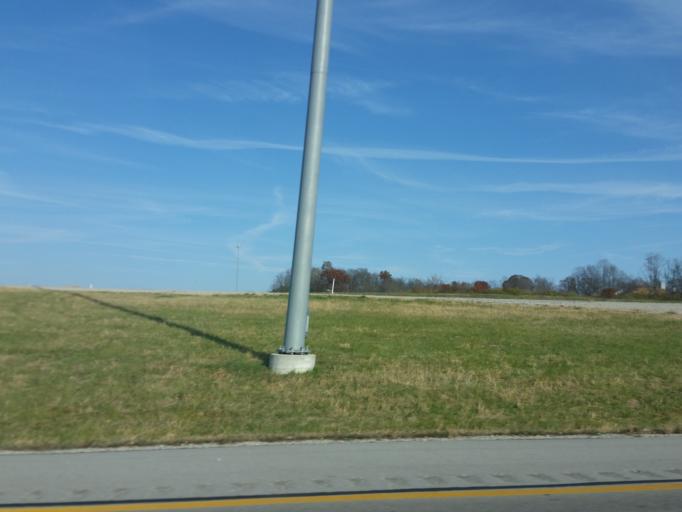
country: US
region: Kentucky
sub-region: Campbell County
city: Highland Heights
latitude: 39.0441
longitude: -84.4589
